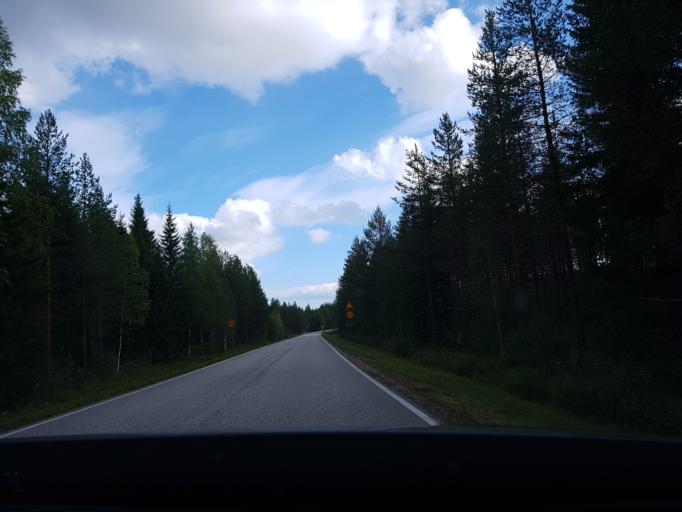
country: FI
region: Kainuu
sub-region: Kehys-Kainuu
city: Kuhmo
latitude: 64.6283
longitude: 29.6933
